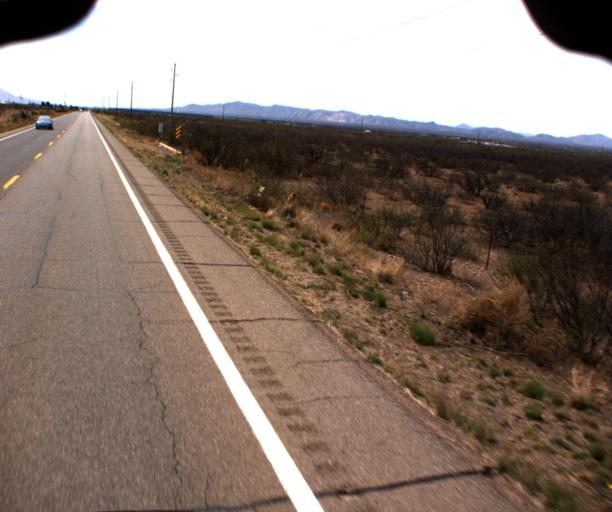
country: US
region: Arizona
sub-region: Cochise County
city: Pirtleville
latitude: 31.3836
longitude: -109.5793
